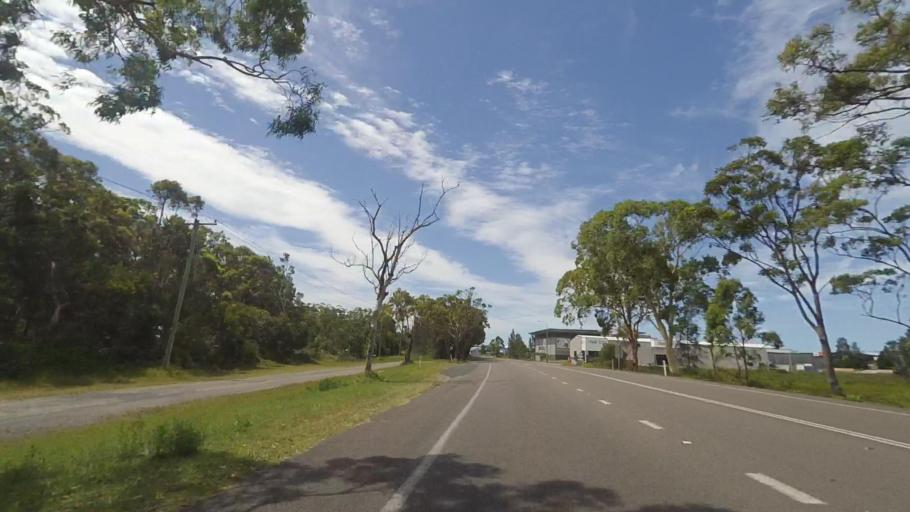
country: AU
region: New South Wales
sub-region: Port Stephens Shire
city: Anna Bay
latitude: -32.7542
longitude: 152.0685
